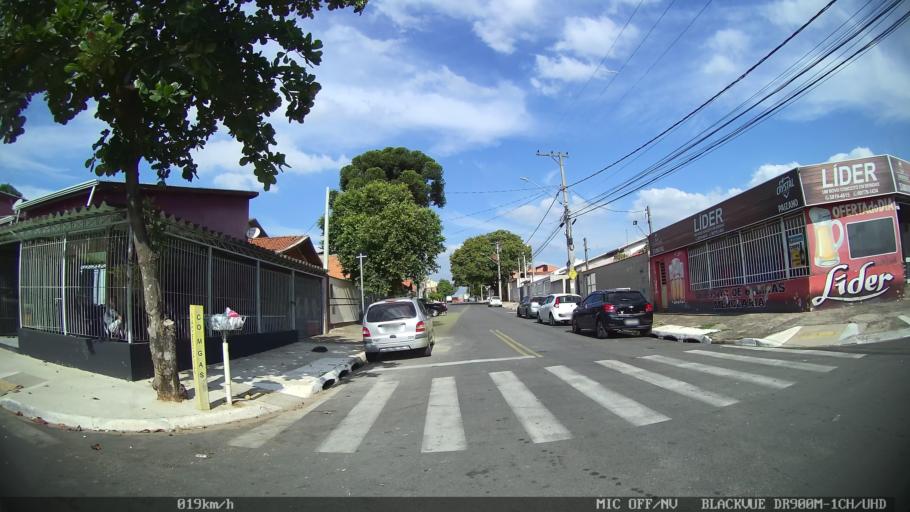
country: BR
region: Sao Paulo
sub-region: Hortolandia
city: Hortolandia
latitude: -22.9059
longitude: -47.2419
